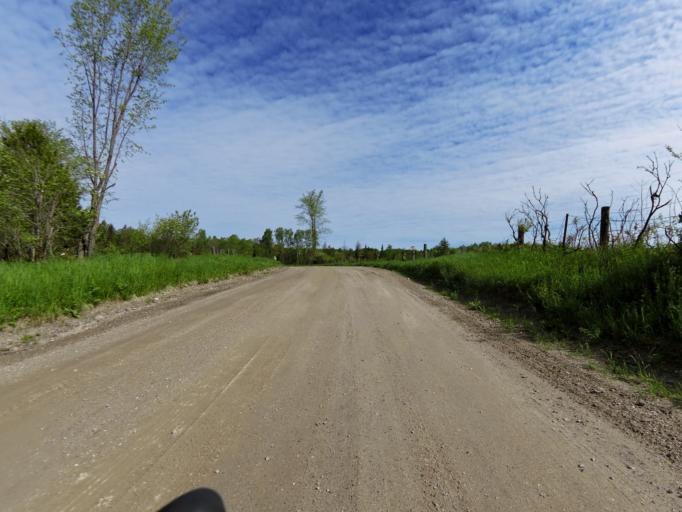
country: CA
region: Quebec
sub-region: Outaouais
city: Wakefield
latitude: 45.6945
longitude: -75.8888
